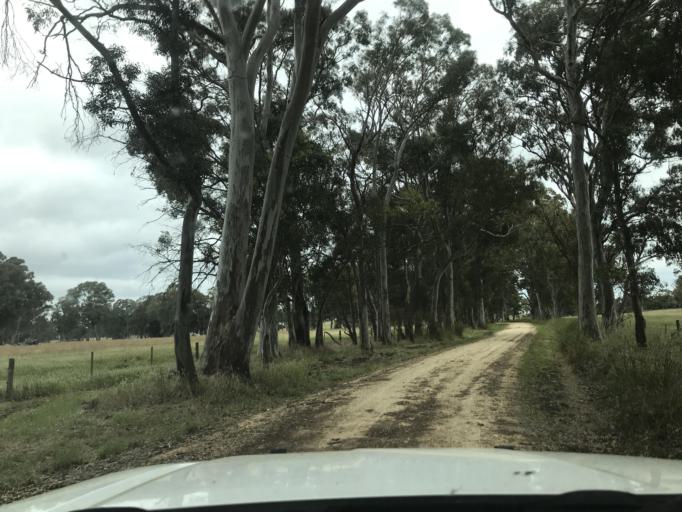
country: AU
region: South Australia
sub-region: Wattle Range
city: Penola
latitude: -37.2705
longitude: 140.9791
